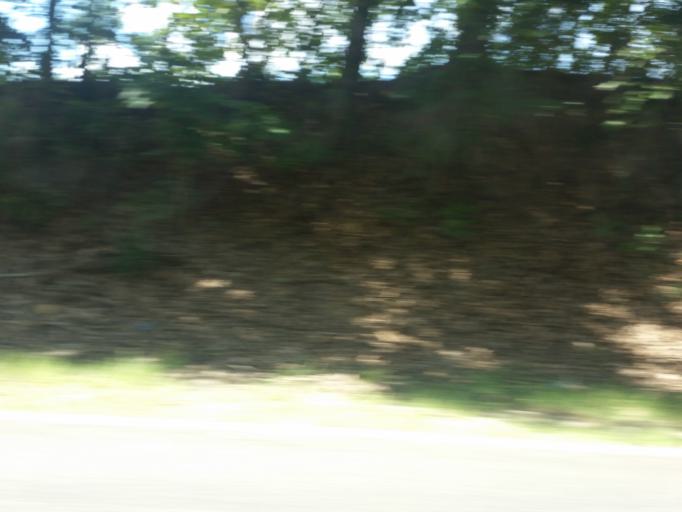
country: US
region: Tennessee
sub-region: Gibson County
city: Milan
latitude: 35.9775
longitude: -88.8021
